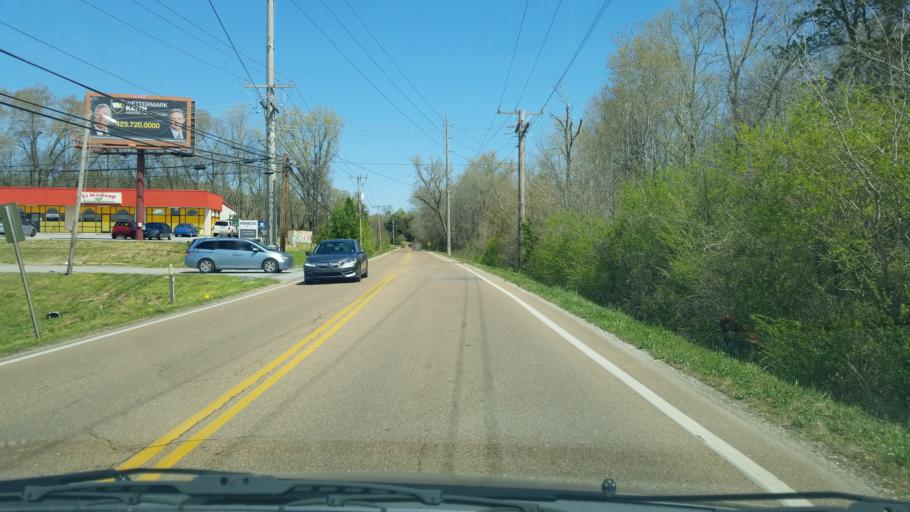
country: US
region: Tennessee
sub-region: Hamilton County
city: Middle Valley
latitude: 35.1742
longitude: -85.2047
